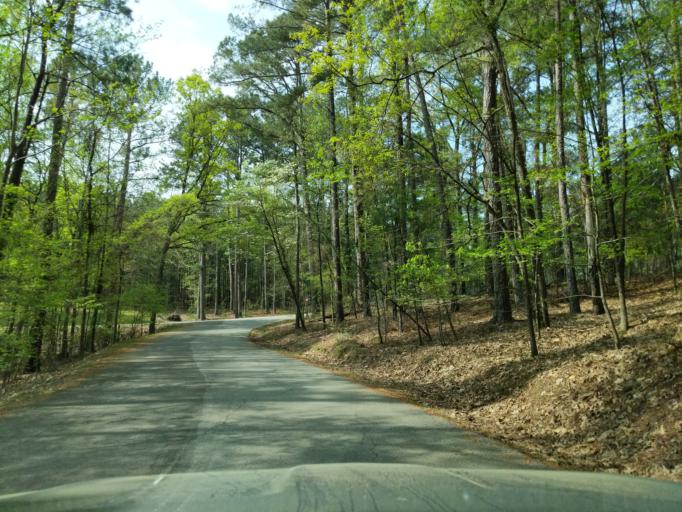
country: US
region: Georgia
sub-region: Lincoln County
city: Lincolnton
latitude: 33.8564
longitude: -82.4144
